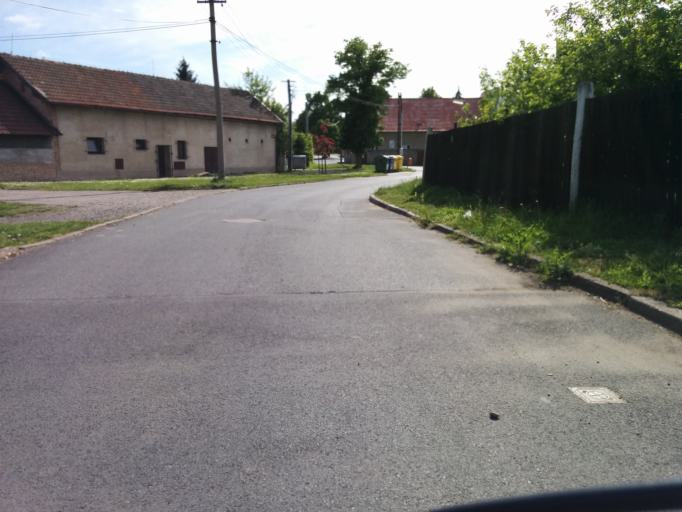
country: CZ
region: Central Bohemia
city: Libis
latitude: 50.2776
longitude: 14.5019
